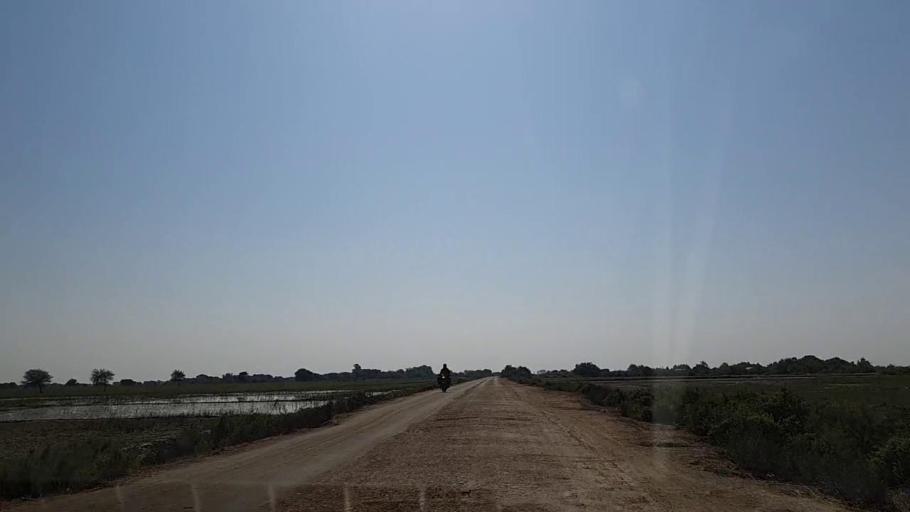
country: PK
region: Sindh
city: Chuhar Jamali
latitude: 24.5196
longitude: 68.0939
